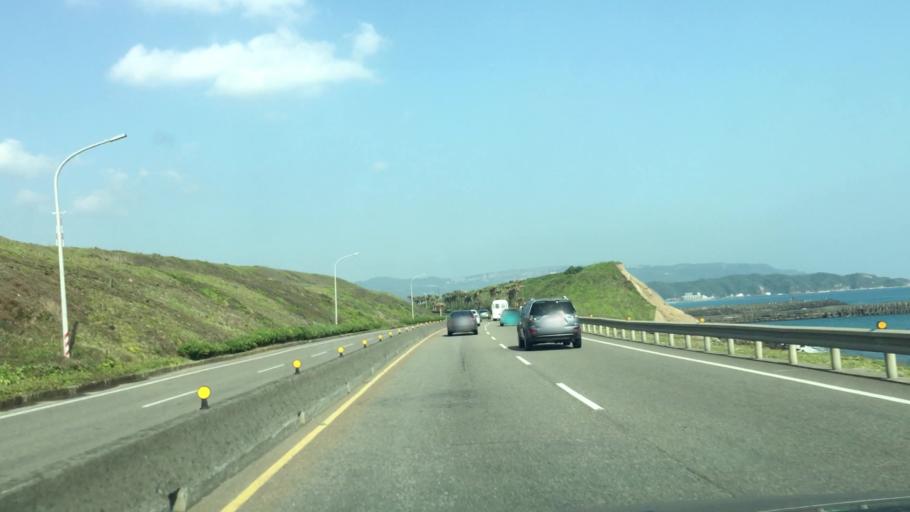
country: TW
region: Taiwan
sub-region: Keelung
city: Keelung
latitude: 25.2037
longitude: 121.6678
